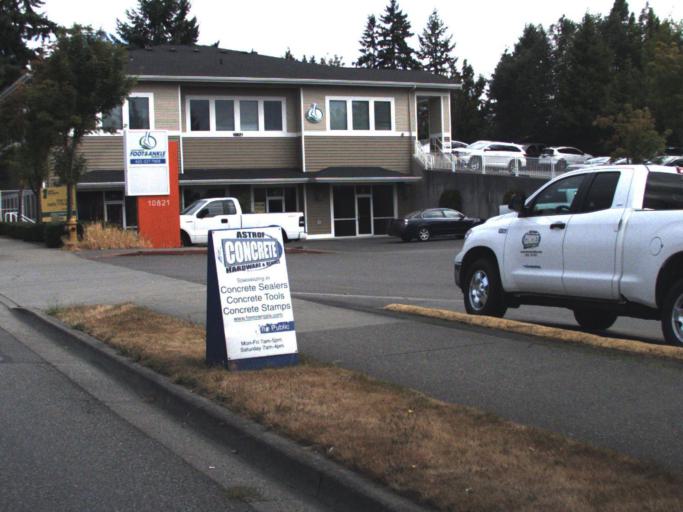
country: US
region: Washington
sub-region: Snohomish County
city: Mill Creek
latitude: 47.8990
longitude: -122.2068
